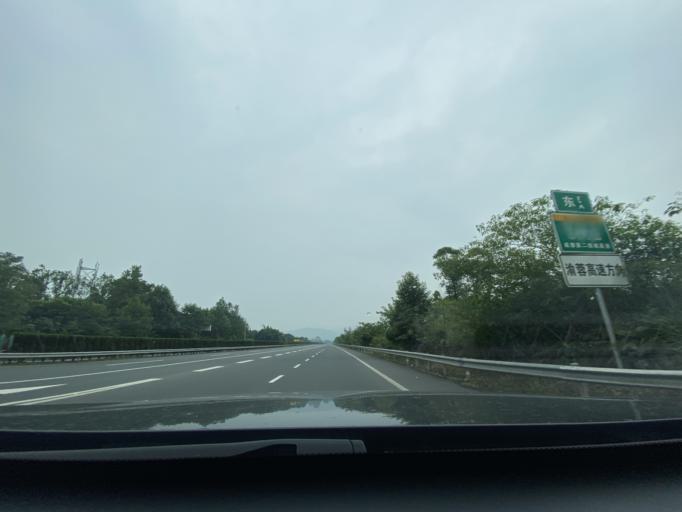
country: CN
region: Sichuan
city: Longquan
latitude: 30.3444
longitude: 104.1244
